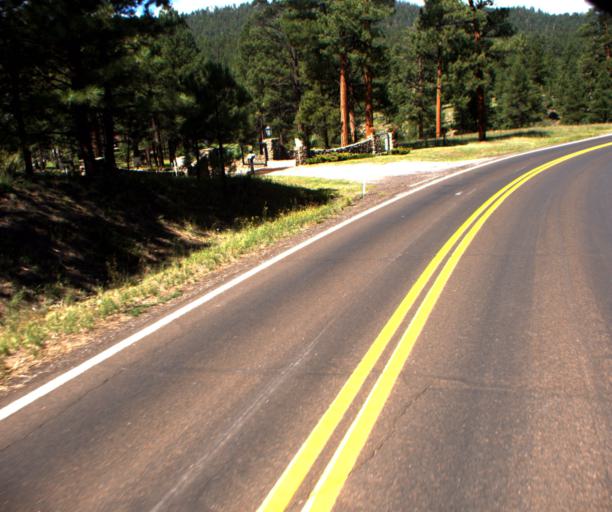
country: US
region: Arizona
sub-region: Apache County
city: Eagar
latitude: 34.0603
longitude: -109.4632
